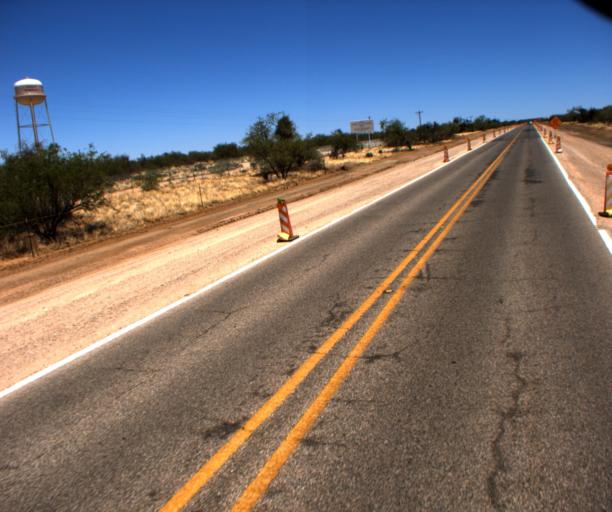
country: US
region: Arizona
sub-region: Pima County
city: Sells
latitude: 31.9887
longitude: -111.7137
